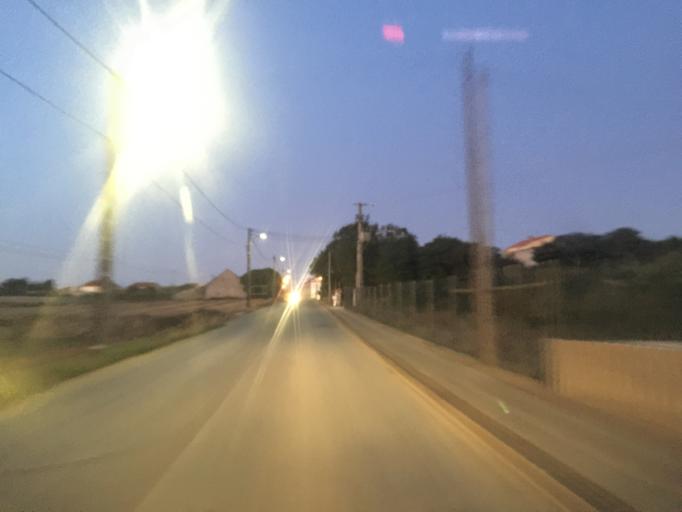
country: PT
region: Lisbon
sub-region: Lourinha
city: Lourinha
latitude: 39.2769
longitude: -9.2607
